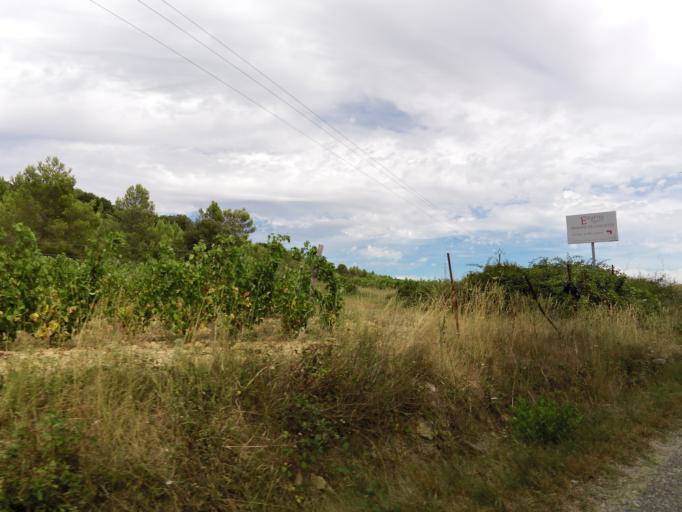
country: FR
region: Languedoc-Roussillon
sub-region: Departement du Gard
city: Congenies
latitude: 43.8045
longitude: 4.1522
